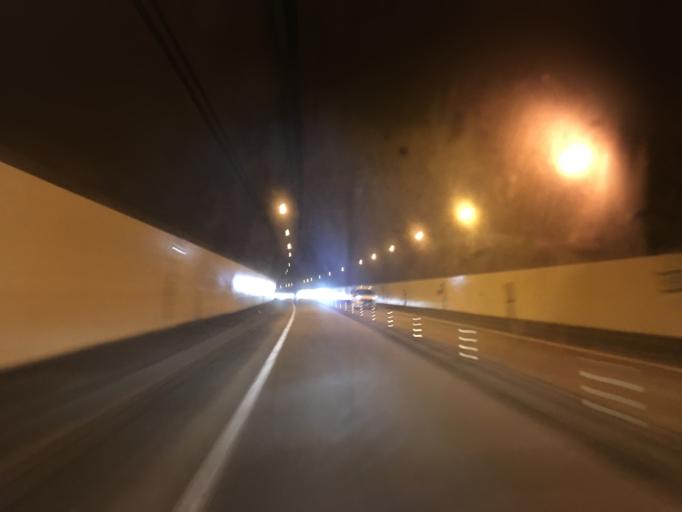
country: JP
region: Miyagi
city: Wakuya
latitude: 38.6314
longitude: 141.2815
